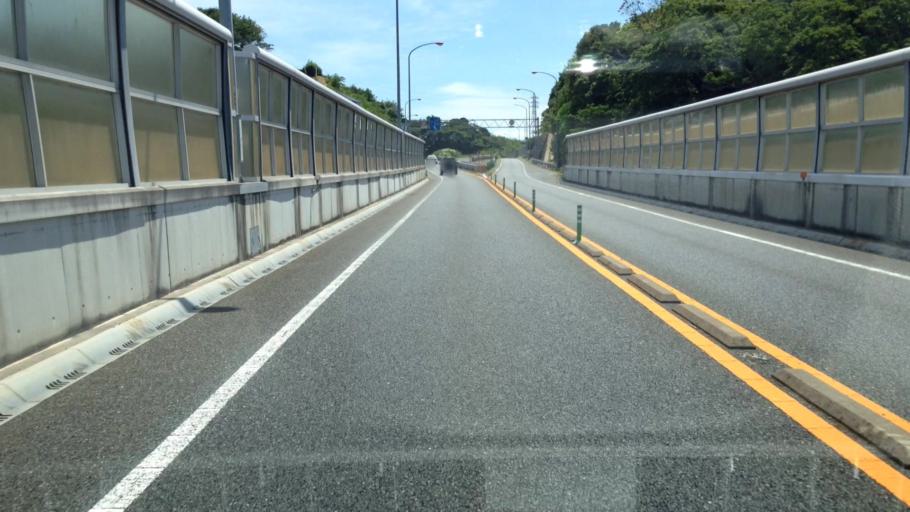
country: JP
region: Kanagawa
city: Yokosuka
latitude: 35.2164
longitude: 139.6375
